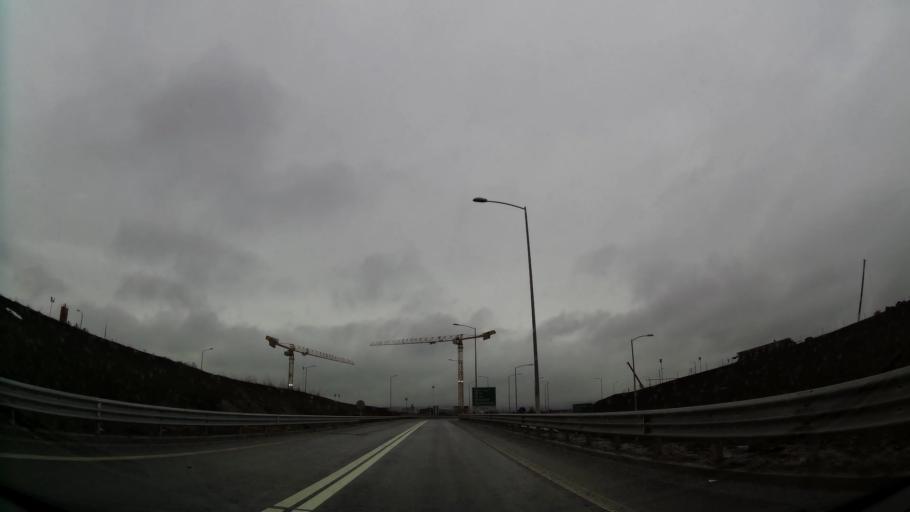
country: XK
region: Ferizaj
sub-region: Komuna e Kacanikut
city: Kacanik
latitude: 42.2764
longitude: 21.2128
